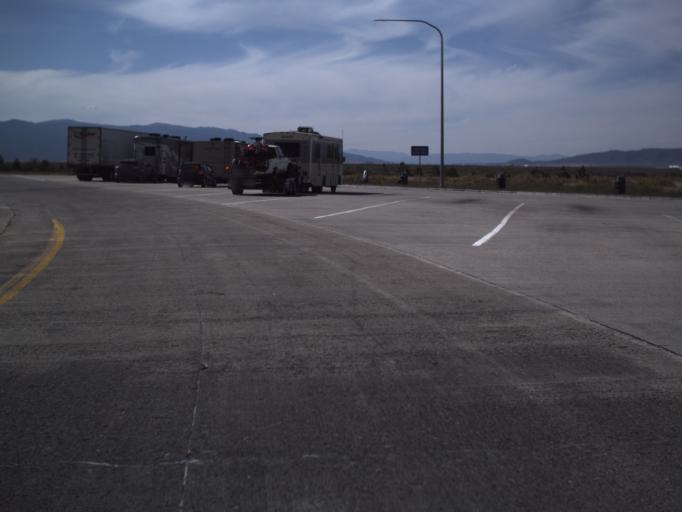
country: US
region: Utah
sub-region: Iron County
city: Parowan
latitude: 37.9831
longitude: -112.7382
